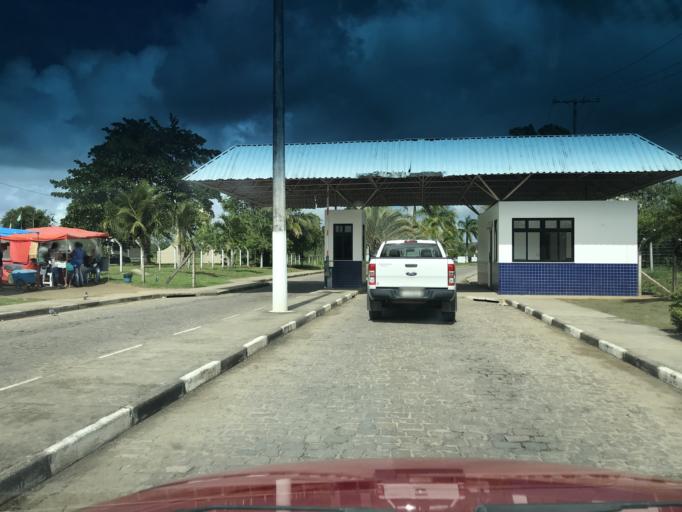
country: BR
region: Bahia
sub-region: Santo Antonio De Jesus
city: Santo Antonio de Jesus
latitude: -12.9792
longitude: -39.2801
